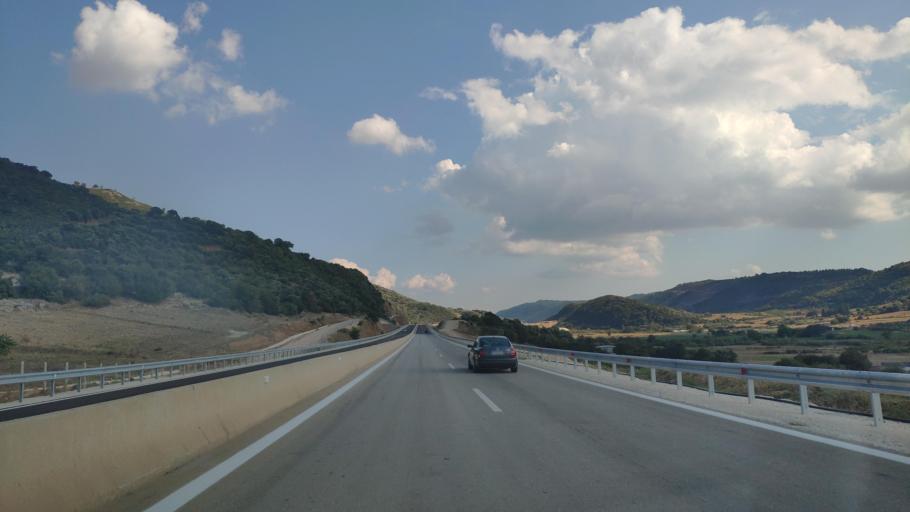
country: GR
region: West Greece
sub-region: Nomos Aitolias kai Akarnanias
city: Katouna
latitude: 38.8021
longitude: 21.1330
